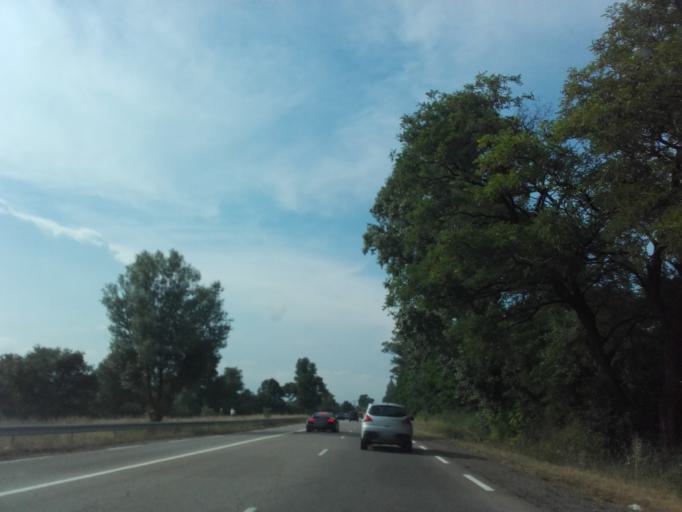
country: FR
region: Rhone-Alpes
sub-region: Departement de l'Ardeche
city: Guilherand-Granges
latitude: 44.9490
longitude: 4.8834
